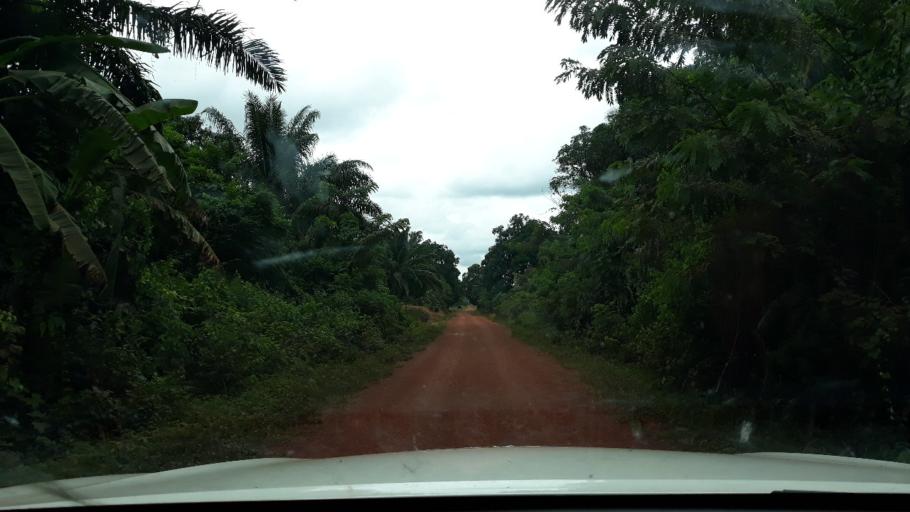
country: CD
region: Equateur
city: Libenge
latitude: 3.6973
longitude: 19.0930
